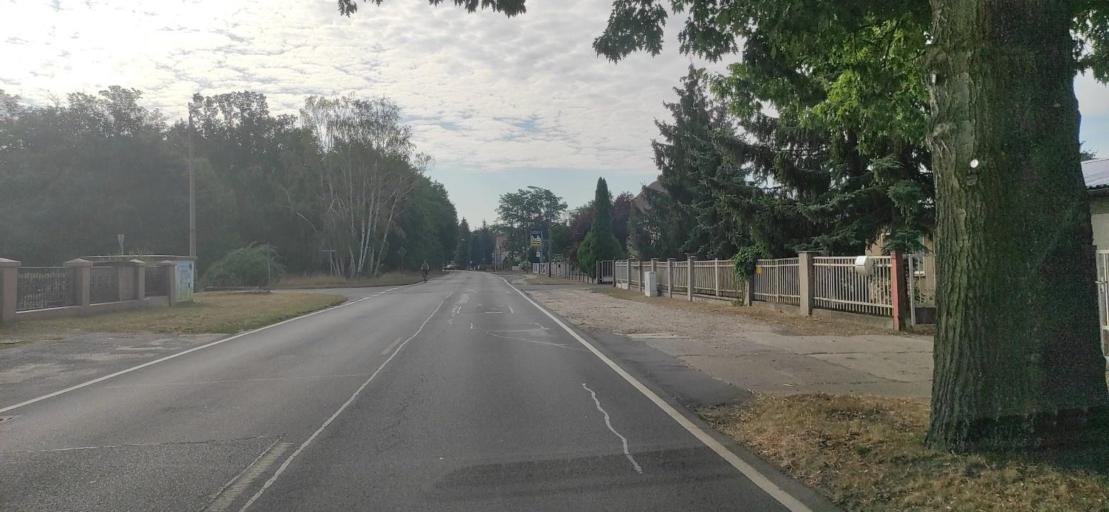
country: DE
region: Brandenburg
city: Forst
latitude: 51.7270
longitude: 14.6475
